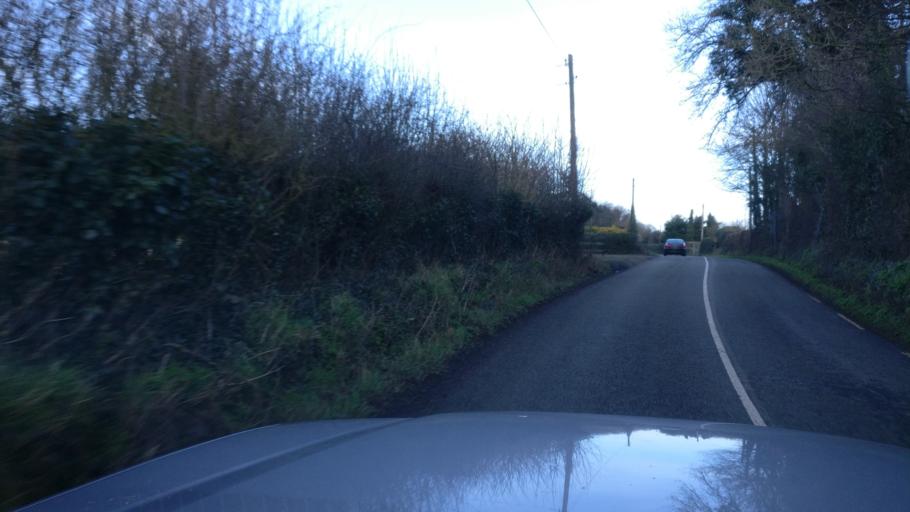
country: IE
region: Leinster
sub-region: Kilkenny
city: Castlecomer
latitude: 52.8459
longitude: -7.1793
